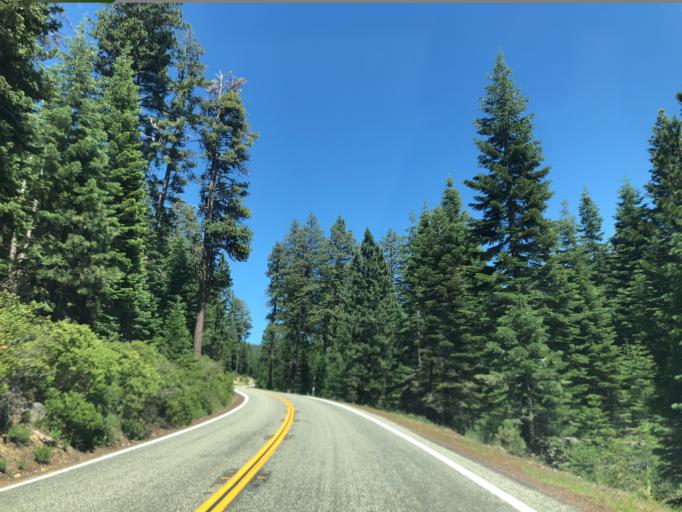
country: US
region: California
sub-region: Shasta County
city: Shingletown
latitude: 40.5383
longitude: -121.5928
